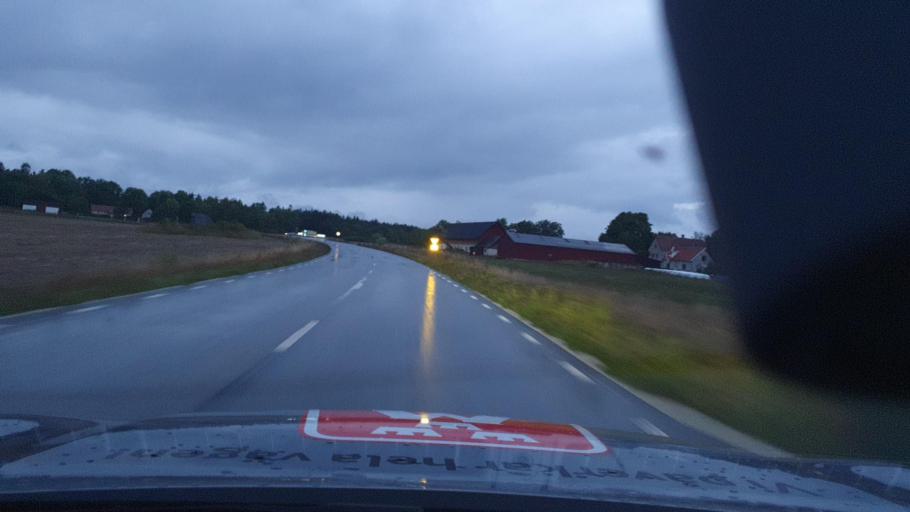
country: SE
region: Gotland
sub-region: Gotland
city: Slite
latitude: 57.7725
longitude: 18.7818
